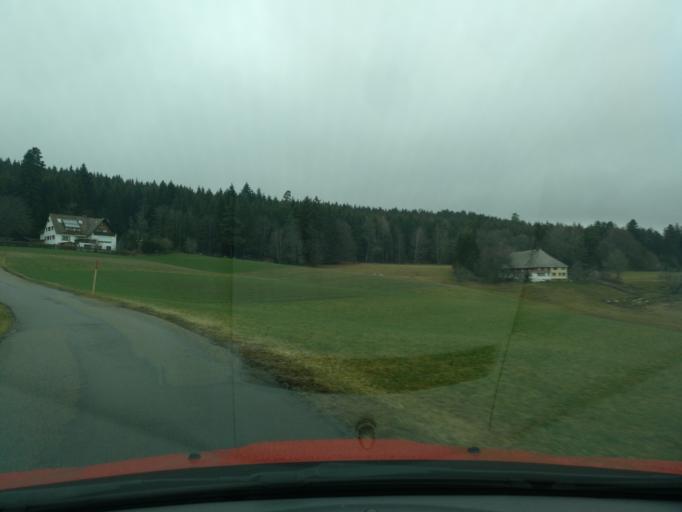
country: DE
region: Baden-Wuerttemberg
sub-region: Freiburg Region
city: Sankt Georgen im Schwarzwald
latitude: 48.1076
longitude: 8.3326
